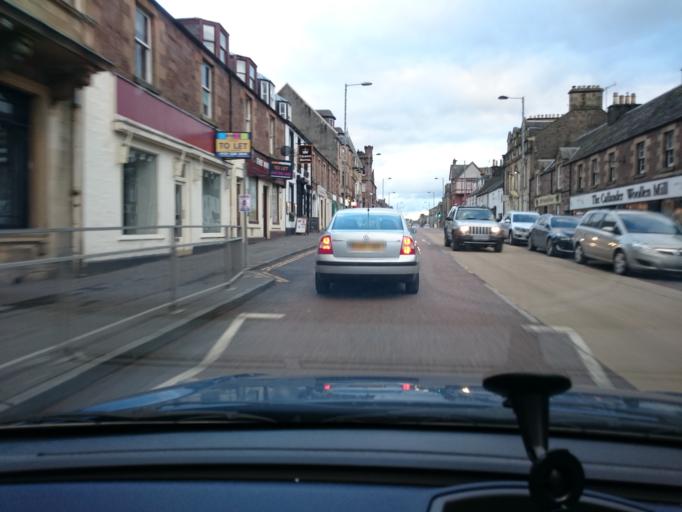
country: GB
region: Scotland
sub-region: Stirling
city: Callander
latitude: 56.2445
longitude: -4.2175
